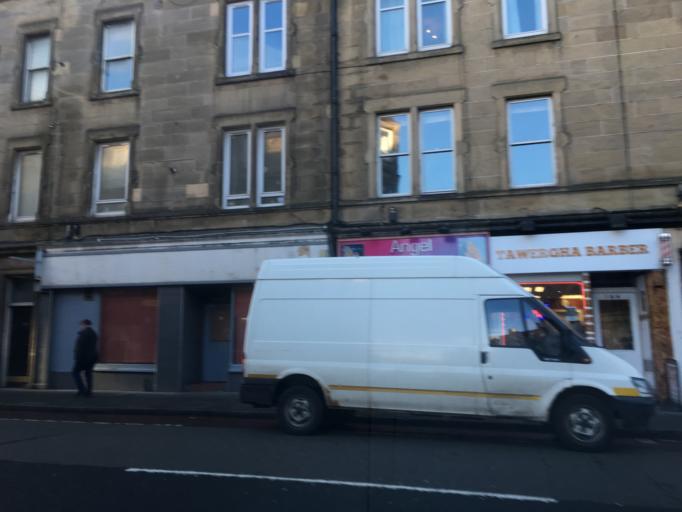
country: GB
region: Scotland
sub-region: Edinburgh
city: Colinton
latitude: 55.9377
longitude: -3.2337
